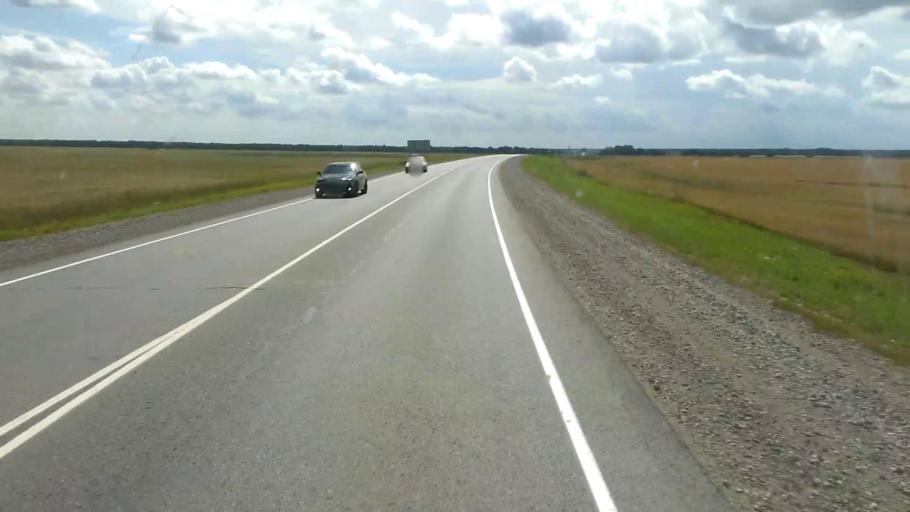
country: RU
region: Altai Krai
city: Troitskoye
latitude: 52.9047
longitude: 84.8302
